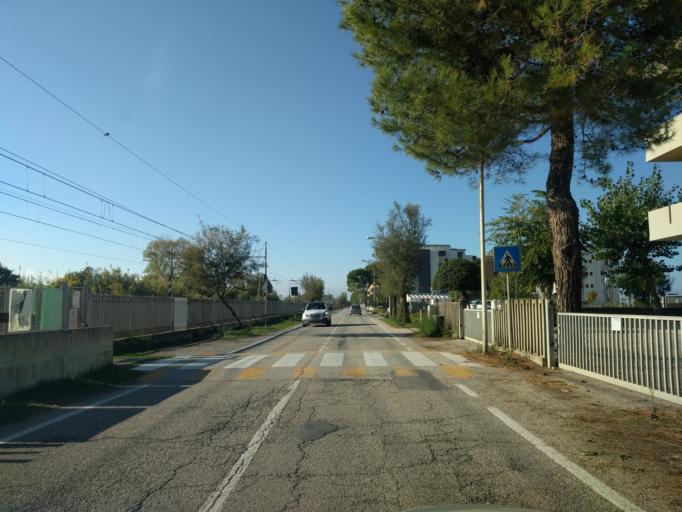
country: IT
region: The Marches
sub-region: Provincia di Pesaro e Urbino
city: Marotta
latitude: 43.7924
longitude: 13.1039
